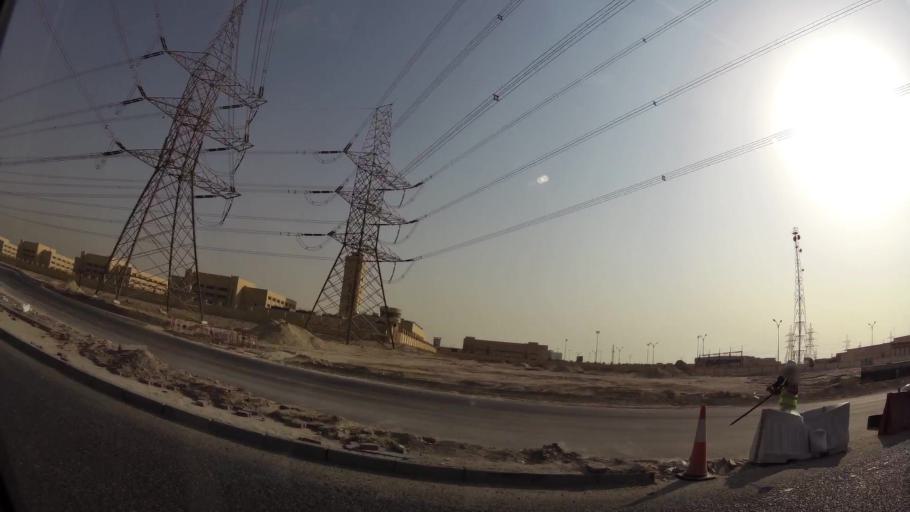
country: KW
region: Al Asimah
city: Ar Rabiyah
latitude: 29.2950
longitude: 47.8571
